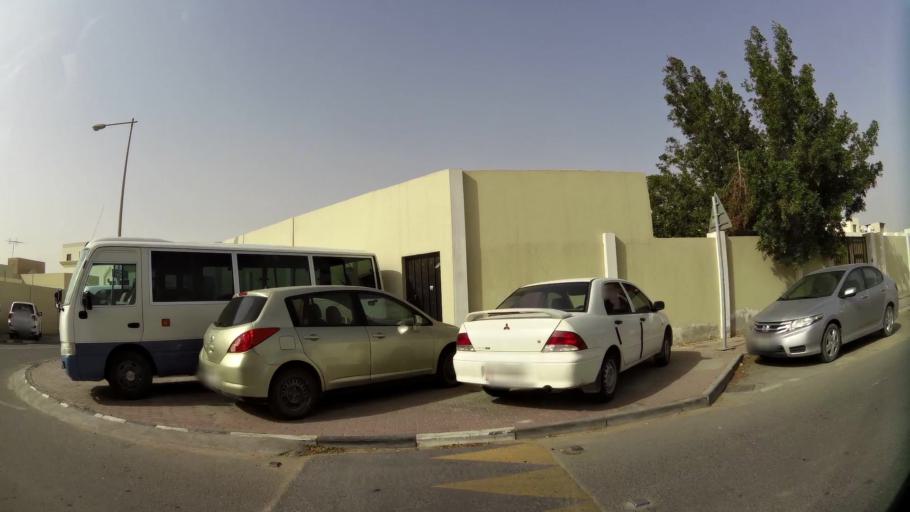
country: QA
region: Baladiyat ar Rayyan
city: Ar Rayyan
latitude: 25.2396
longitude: 51.4330
